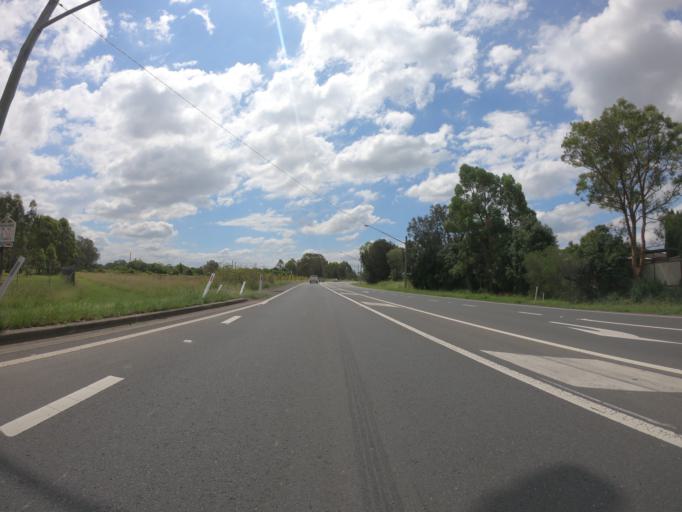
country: AU
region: New South Wales
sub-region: Blacktown
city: Mount Druitt
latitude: -33.8033
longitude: 150.7692
